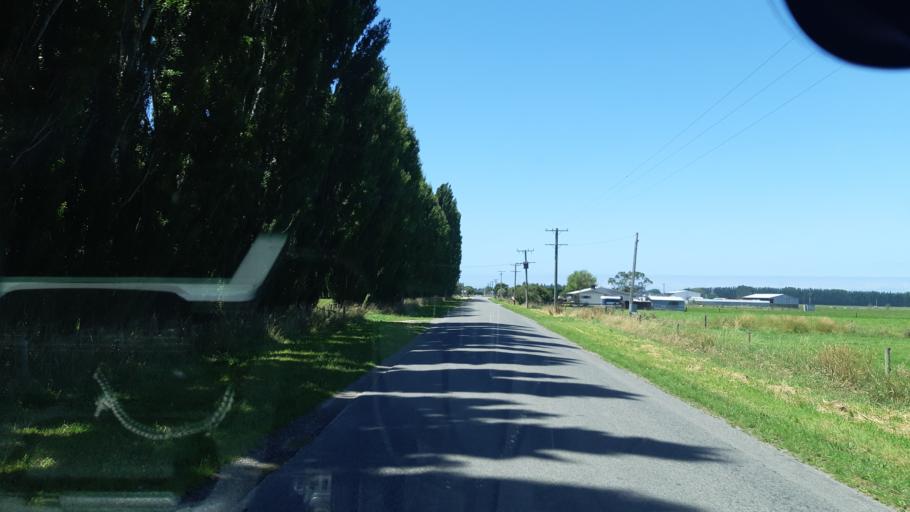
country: NZ
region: Canterbury
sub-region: Waimakariri District
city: Woodend
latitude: -43.2804
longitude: 172.6582
